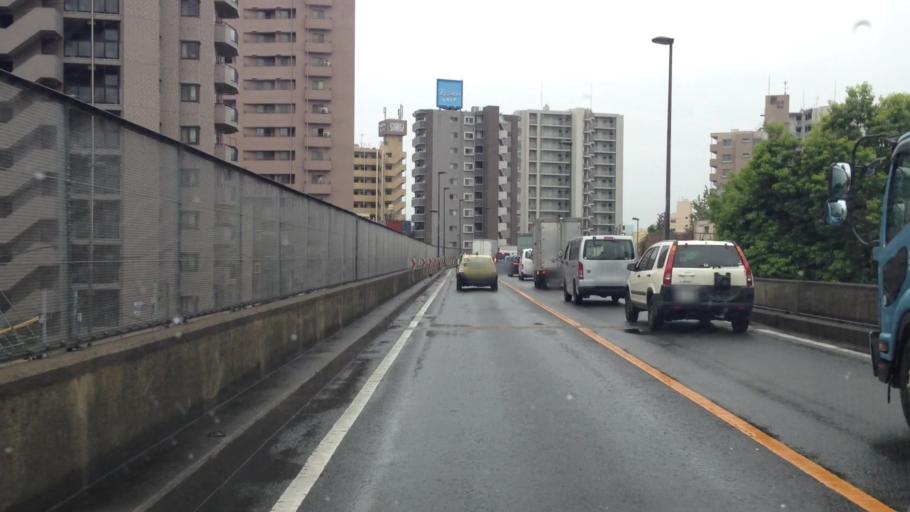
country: JP
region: Saitama
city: Soka
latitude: 35.7380
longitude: 139.7971
